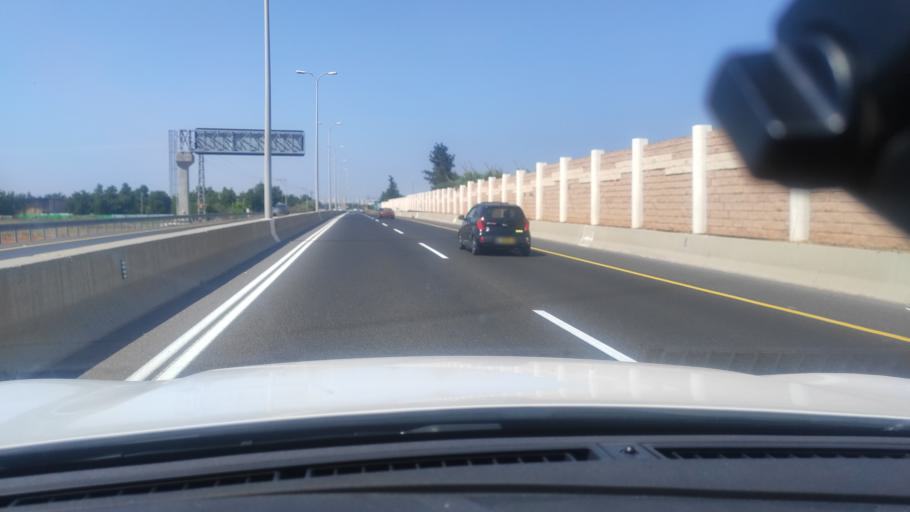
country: IL
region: Central District
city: Kfar Saba
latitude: 32.1557
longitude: 34.9247
